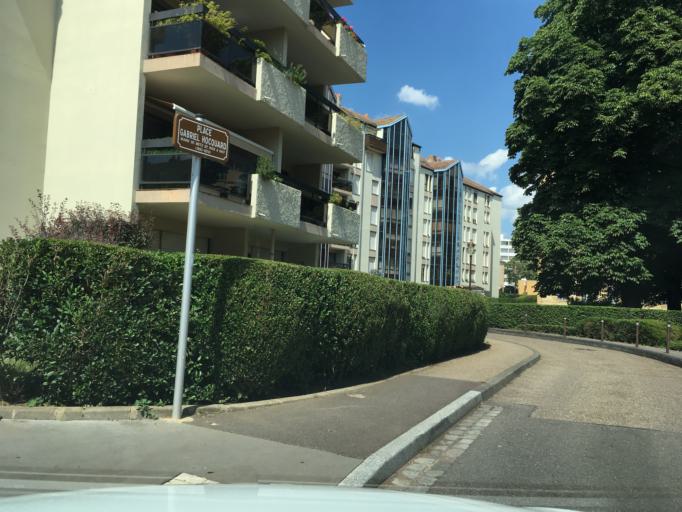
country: FR
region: Lorraine
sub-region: Departement de la Moselle
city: Metz
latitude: 49.1244
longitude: 6.1748
